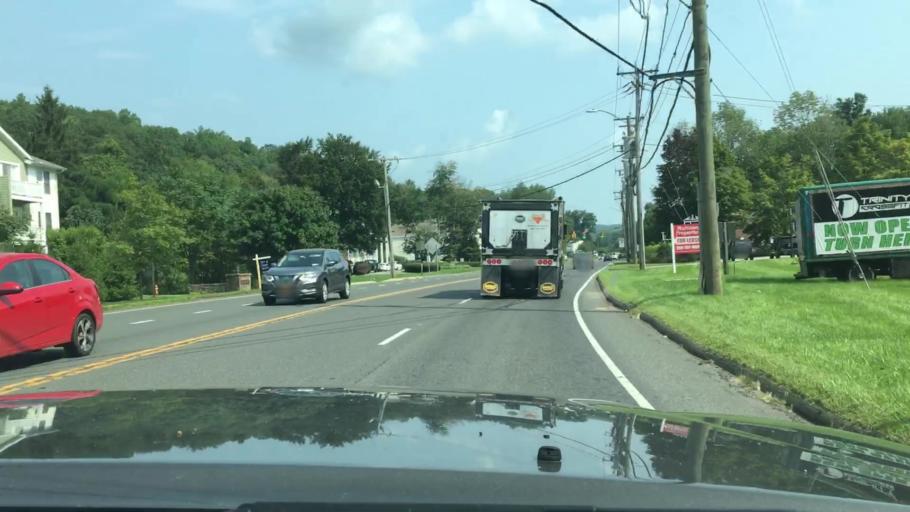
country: US
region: Connecticut
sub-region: Fairfield County
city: Ridgefield
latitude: 41.3226
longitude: -73.4758
